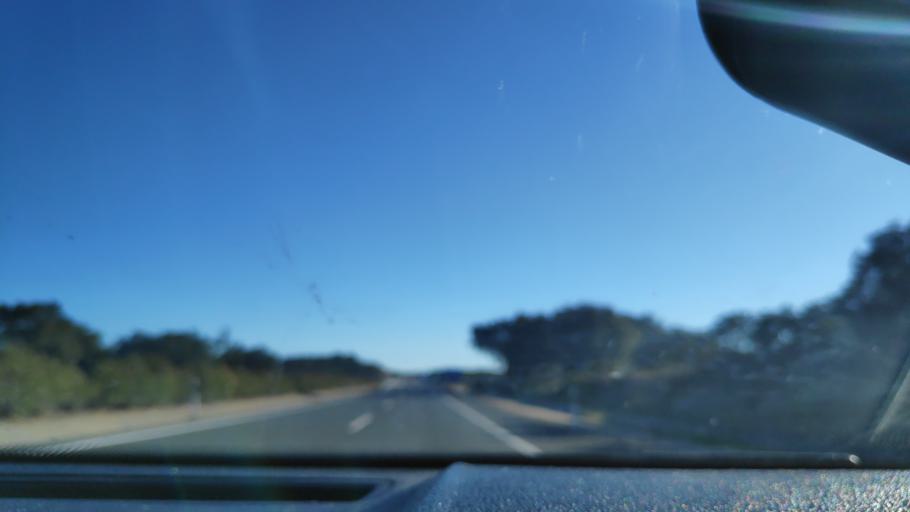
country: ES
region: Andalusia
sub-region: Provincia de Huelva
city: Santa Olalla del Cala
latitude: 37.9609
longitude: -6.2339
